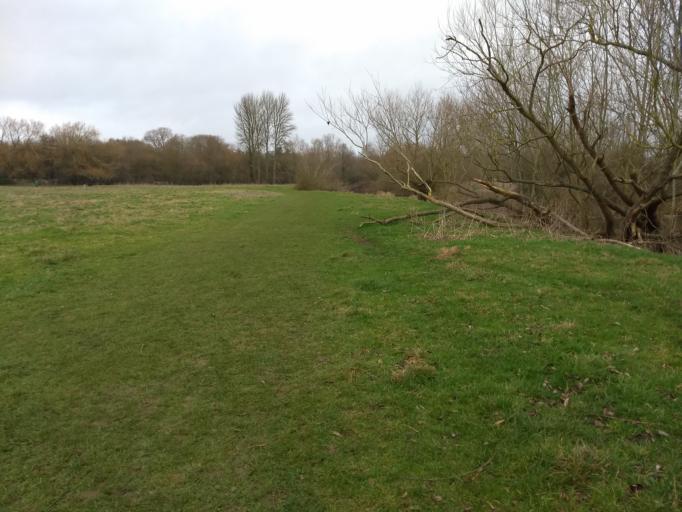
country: GB
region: England
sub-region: Bedford
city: Odell
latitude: 52.2046
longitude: -0.5896
